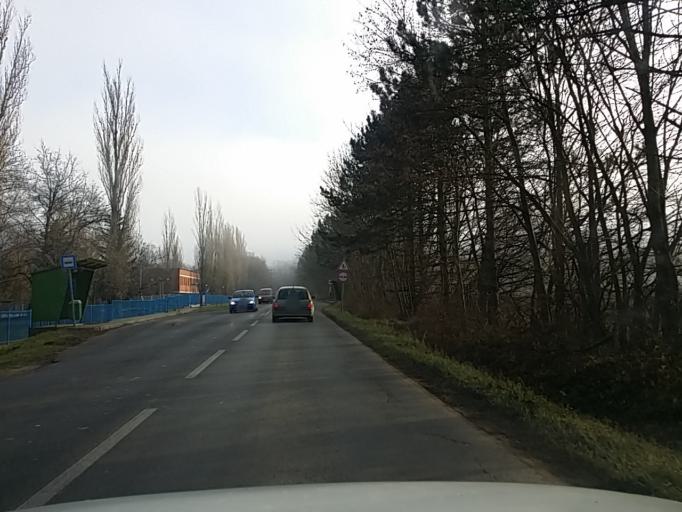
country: HU
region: Pest
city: Budakeszi
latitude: 47.5503
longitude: 18.9333
